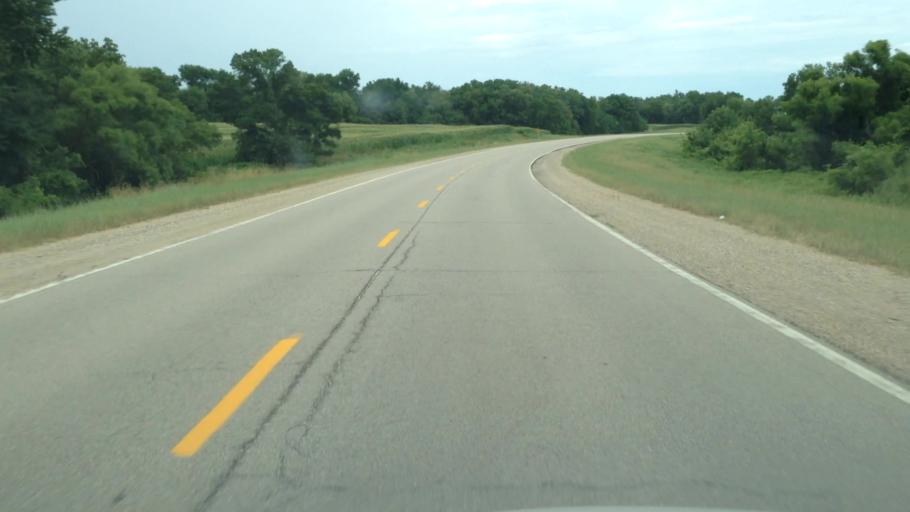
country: US
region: Kansas
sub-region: Jefferson County
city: Oskaloosa
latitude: 39.0943
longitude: -95.4773
